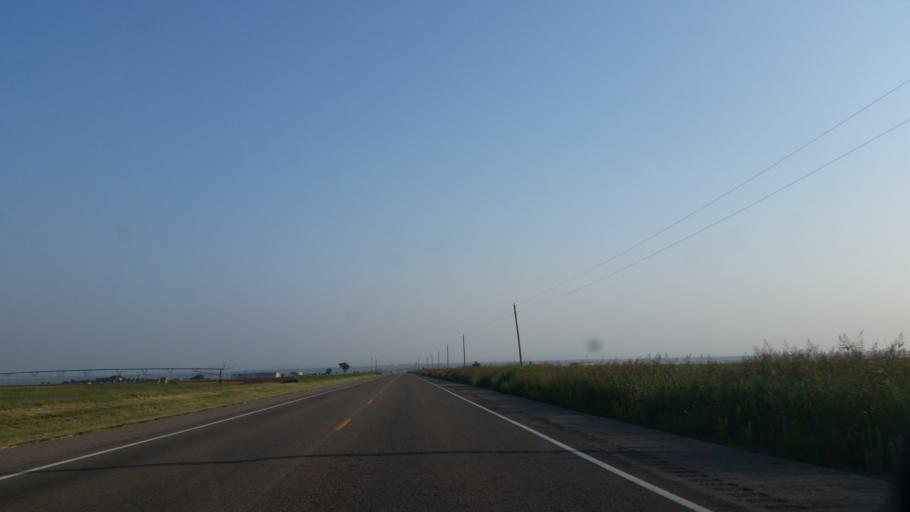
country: US
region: New Mexico
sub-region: Curry County
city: Clovis
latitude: 34.5091
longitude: -103.1962
